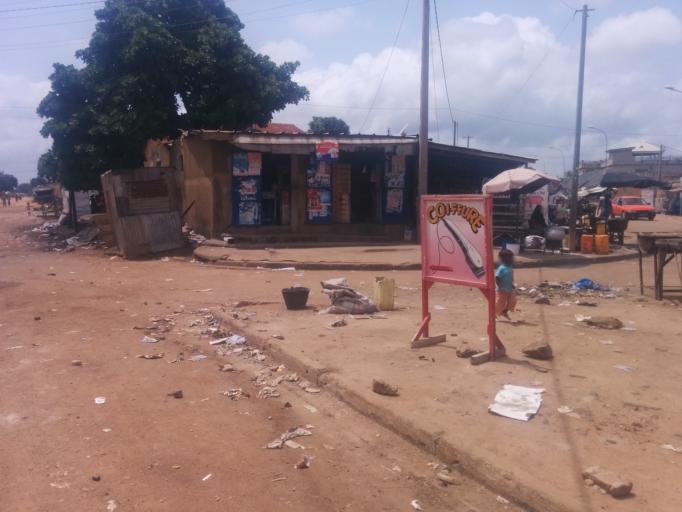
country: CI
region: Vallee du Bandama
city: Bouake
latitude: 7.6900
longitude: -5.0357
